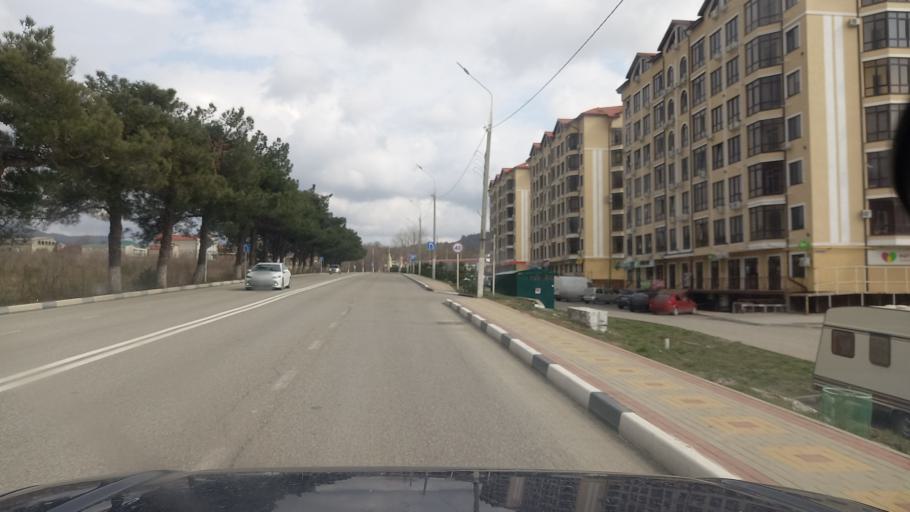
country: RU
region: Krasnodarskiy
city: Gelendzhik
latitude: 44.5556
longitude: 38.1077
